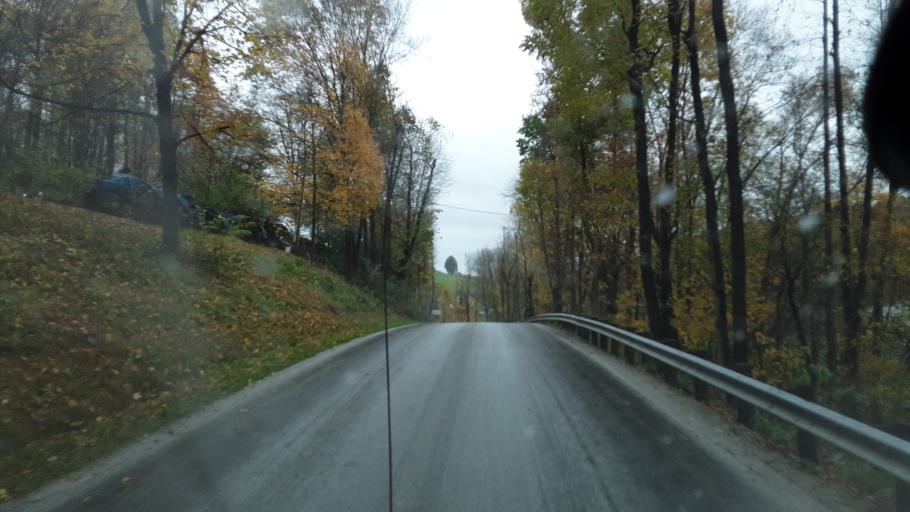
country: US
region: Ohio
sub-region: Coshocton County
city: West Lafayette
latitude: 40.3955
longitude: -81.7634
